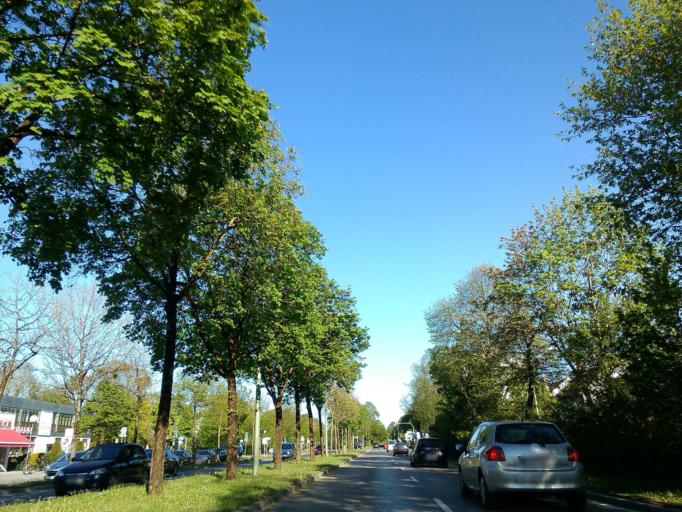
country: DE
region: Bavaria
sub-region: Upper Bavaria
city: Neuried
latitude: 48.0873
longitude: 11.4838
